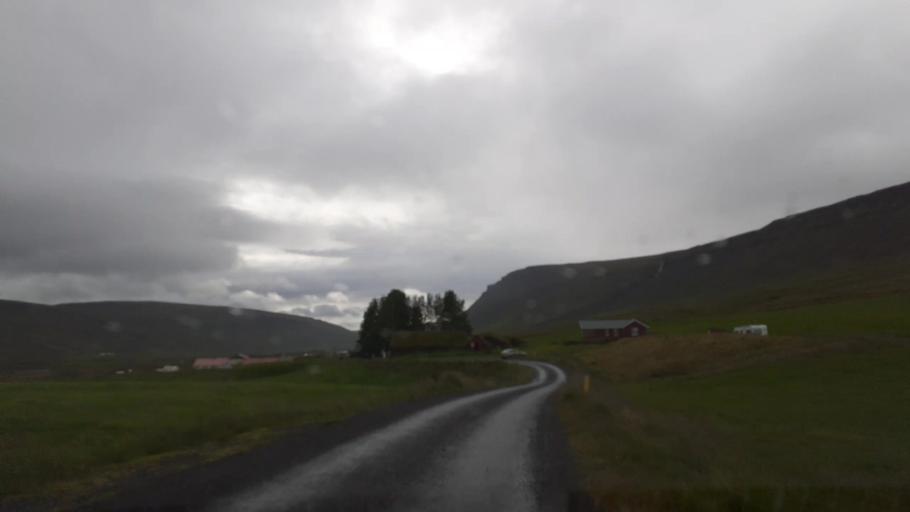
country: IS
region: East
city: Egilsstadir
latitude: 65.6167
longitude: -15.0957
